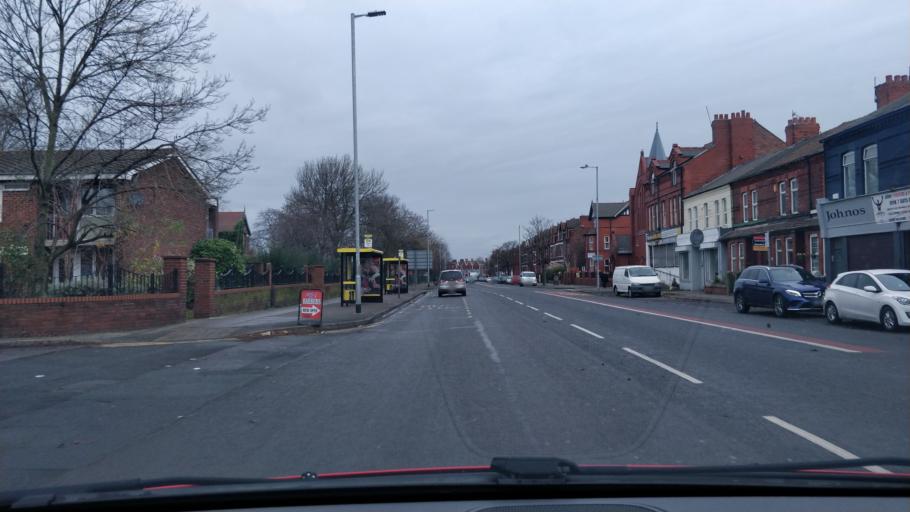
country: GB
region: England
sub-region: Sefton
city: Litherland
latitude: 53.4550
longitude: -2.9917
